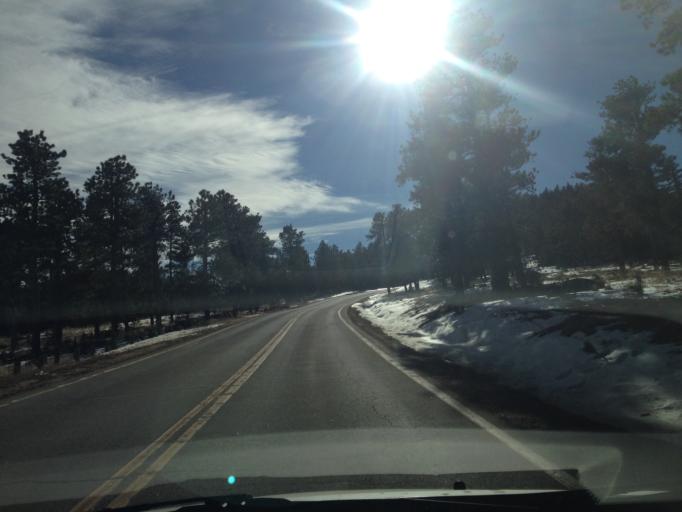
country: US
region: Colorado
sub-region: Boulder County
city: Boulder
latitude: 39.9879
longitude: -105.3201
